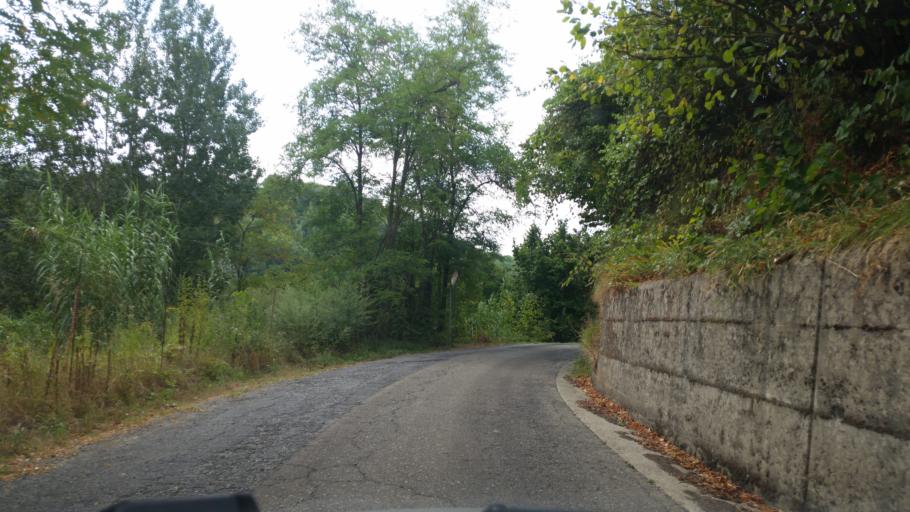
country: IT
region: Piedmont
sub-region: Provincia di Cuneo
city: Camo
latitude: 44.6846
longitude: 8.1992
